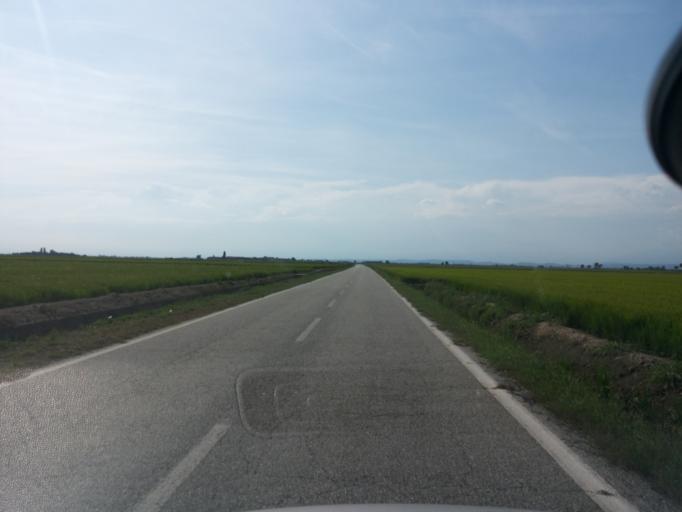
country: IT
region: Piedmont
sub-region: Provincia di Vercelli
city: Salasco
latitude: 45.2965
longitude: 8.2807
